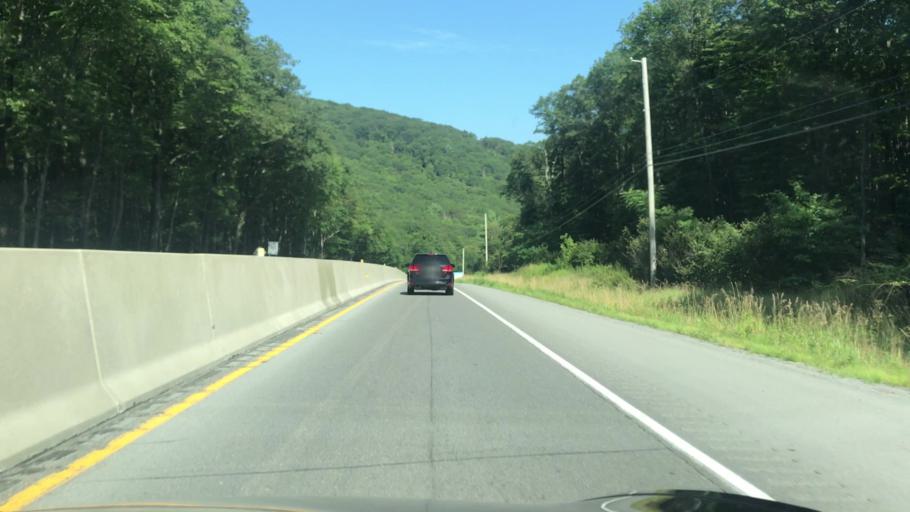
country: US
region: Pennsylvania
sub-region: Lycoming County
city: Montoursville
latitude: 41.2172
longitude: -76.9319
